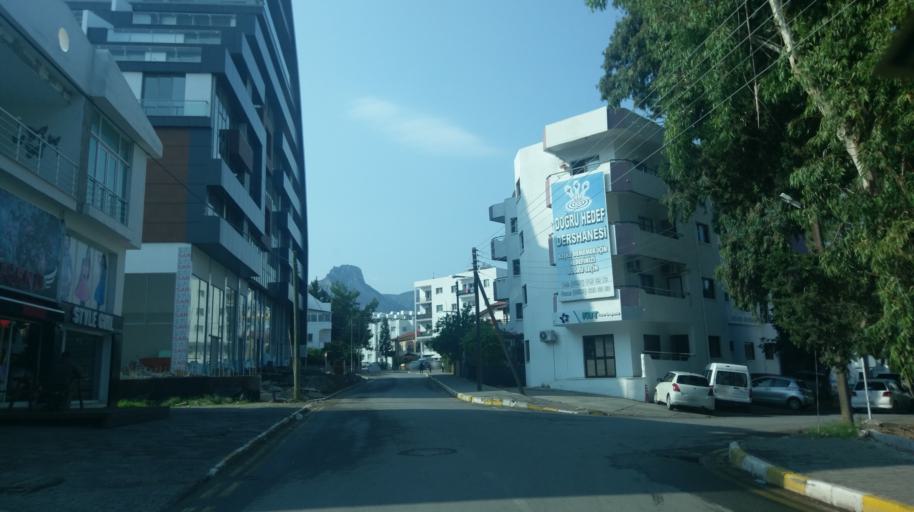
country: CY
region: Keryneia
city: Kyrenia
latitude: 35.3340
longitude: 33.3167
